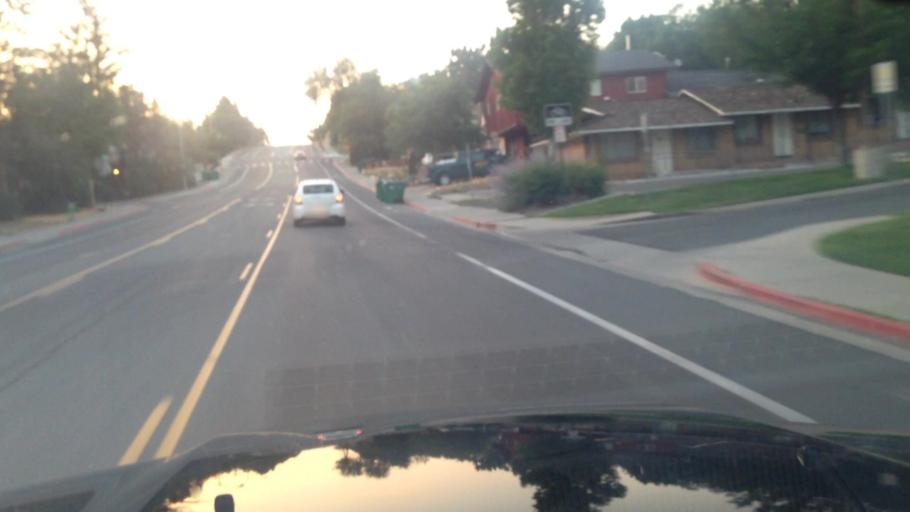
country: US
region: Nevada
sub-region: Washoe County
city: Reno
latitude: 39.5398
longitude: -119.8192
